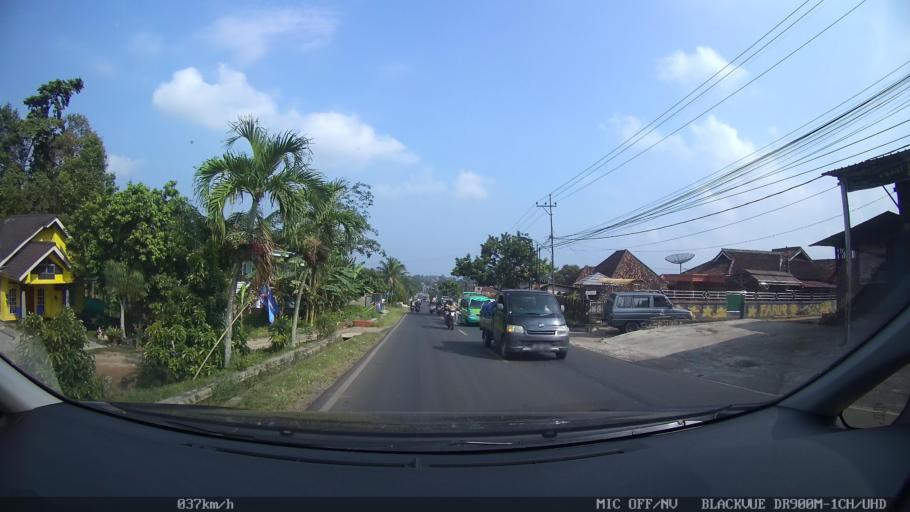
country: ID
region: Lampung
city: Kedaton
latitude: -5.3853
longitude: 105.2014
